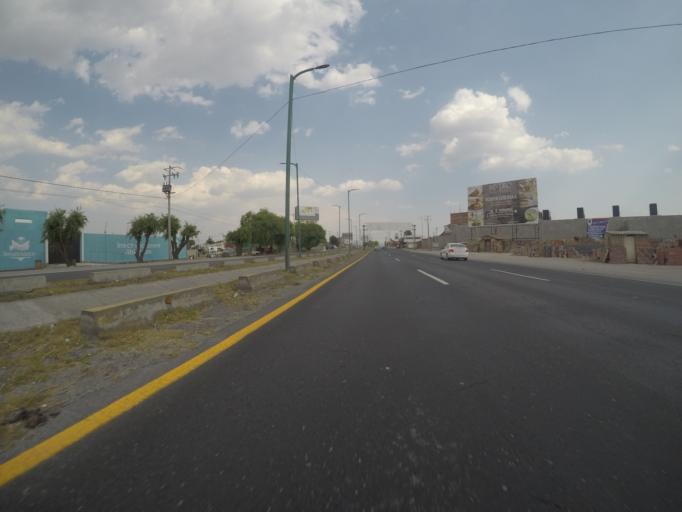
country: MX
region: Mexico
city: San Mateo Mexicaltzingo
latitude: 19.2069
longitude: -99.5897
